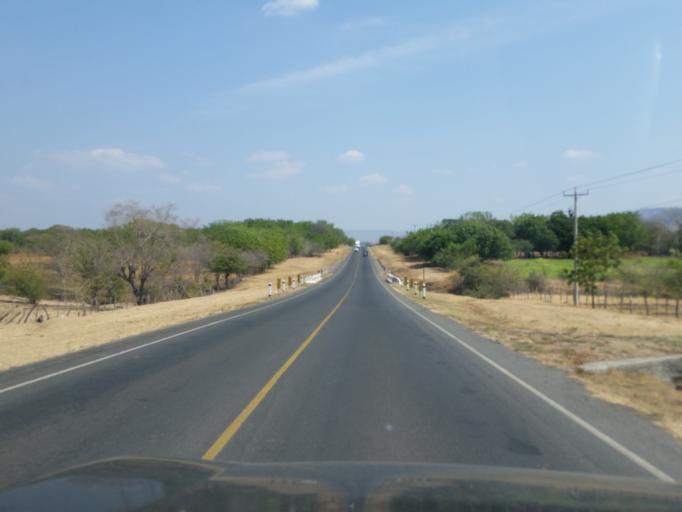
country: NI
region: Managua
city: Tipitapa
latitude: 12.3764
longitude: -86.0461
